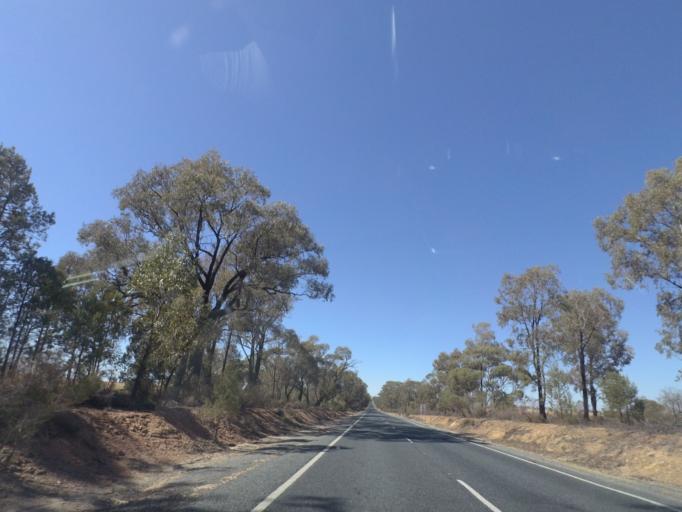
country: AU
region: New South Wales
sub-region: Bland
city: West Wyalong
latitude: -34.1458
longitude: 147.1193
